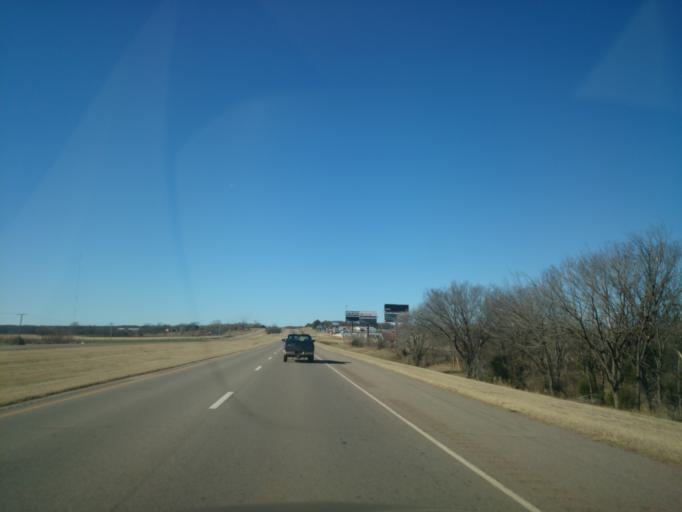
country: US
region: Oklahoma
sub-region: Payne County
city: Stillwater
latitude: 36.1163
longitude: -97.1709
